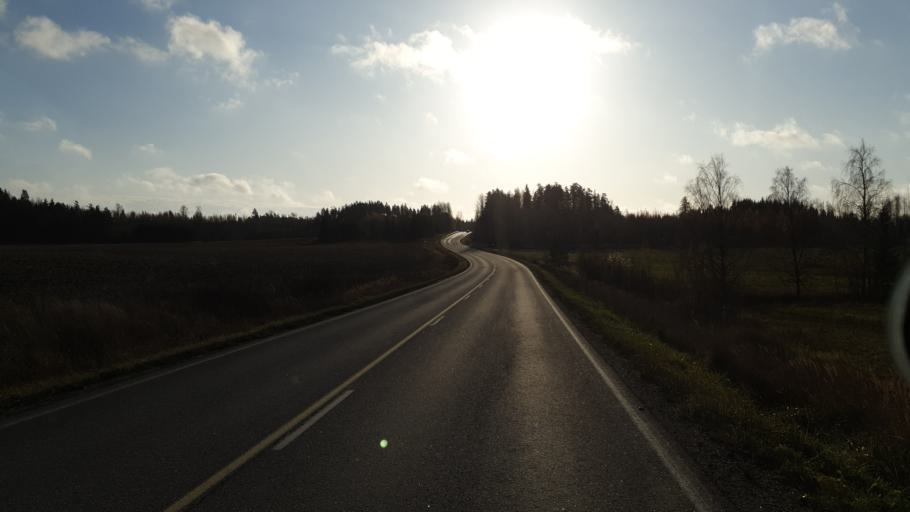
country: FI
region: Uusimaa
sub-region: Helsinki
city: Lohja
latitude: 60.2257
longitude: 24.1664
